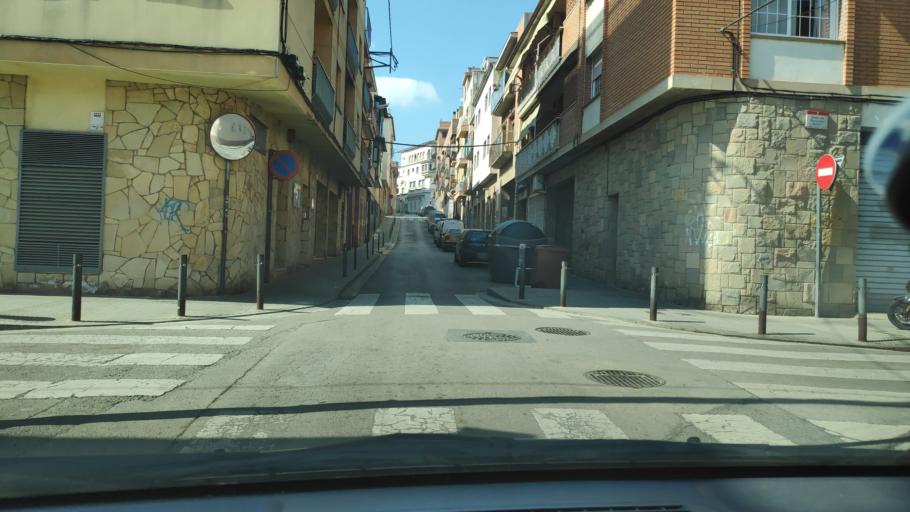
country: ES
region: Catalonia
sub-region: Provincia de Barcelona
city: Mollet del Valles
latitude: 41.5419
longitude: 2.2168
